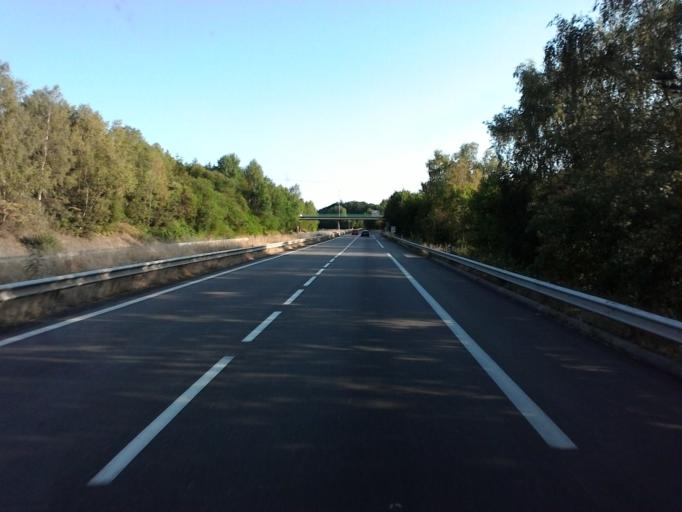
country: FR
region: Lorraine
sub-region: Departement des Vosges
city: Epinal
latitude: 48.1781
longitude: 6.4839
